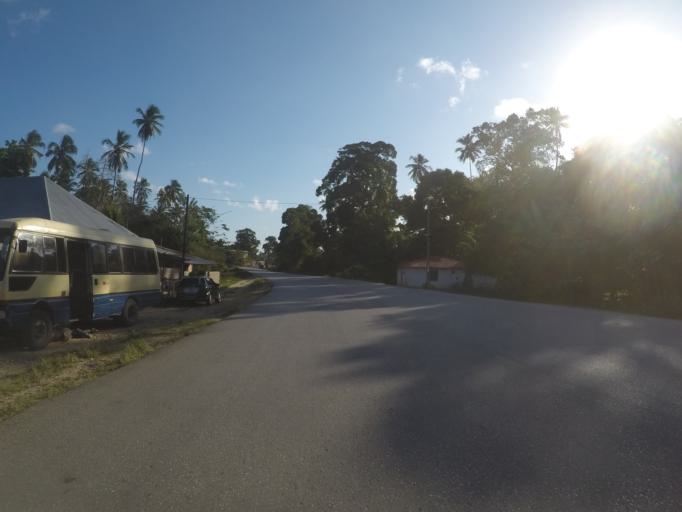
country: TZ
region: Zanzibar Central/South
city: Koani
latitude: -6.1425
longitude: 39.2750
